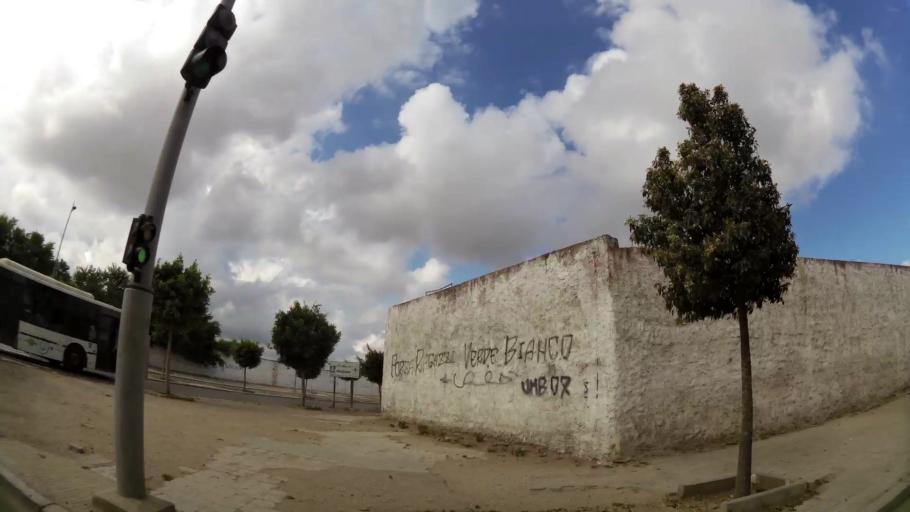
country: MA
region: Gharb-Chrarda-Beni Hssen
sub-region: Kenitra Province
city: Kenitra
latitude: 34.2592
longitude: -6.5653
